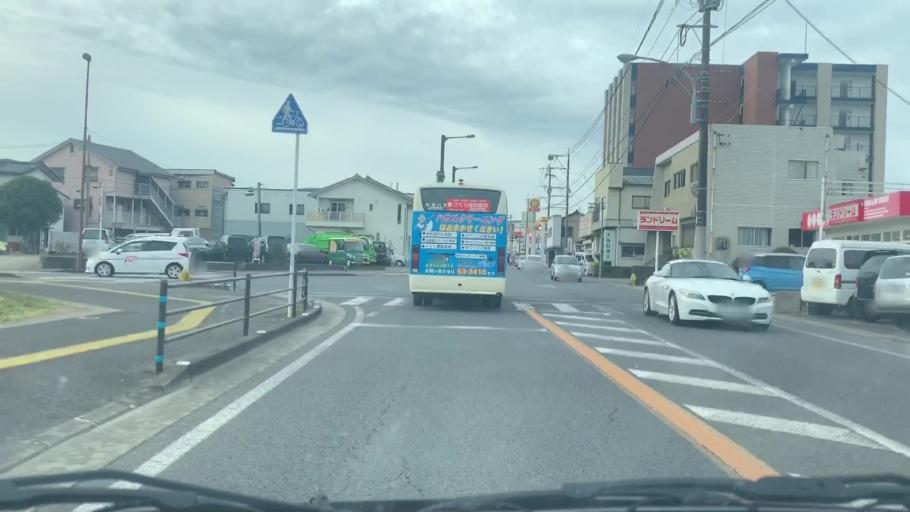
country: JP
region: Saga Prefecture
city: Ureshinomachi-shimojuku
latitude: 33.1028
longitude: 129.9928
